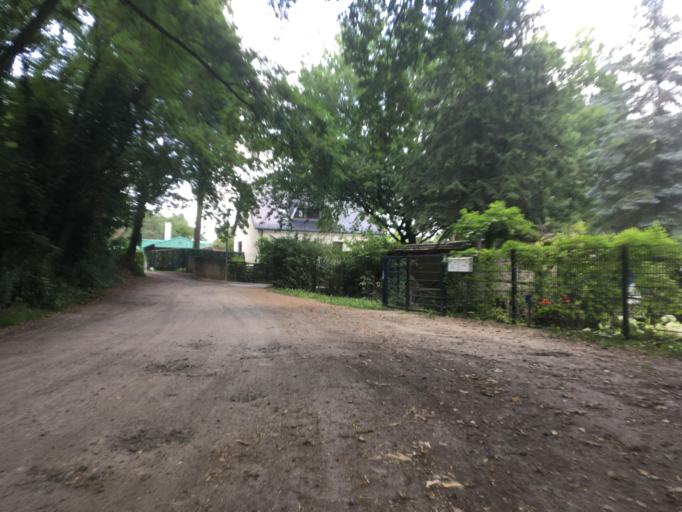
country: DE
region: Brandenburg
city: Wildau
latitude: 52.3403
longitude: 13.6252
